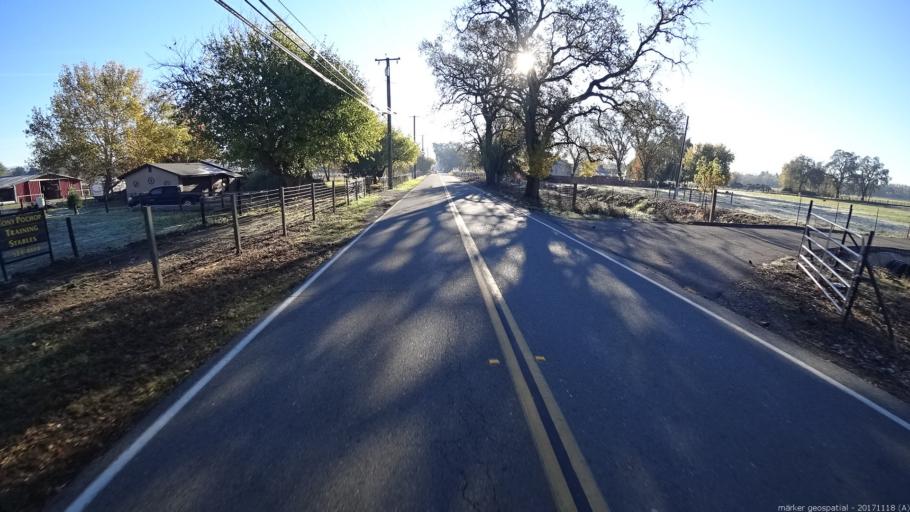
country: US
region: California
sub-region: Shasta County
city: Anderson
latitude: 40.4502
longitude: -122.2658
